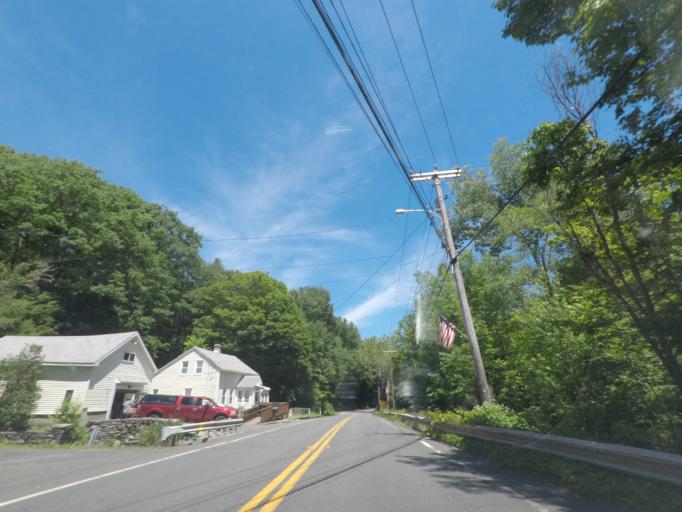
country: US
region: Massachusetts
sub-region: Berkshire County
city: Becket
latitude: 42.2789
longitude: -72.9895
